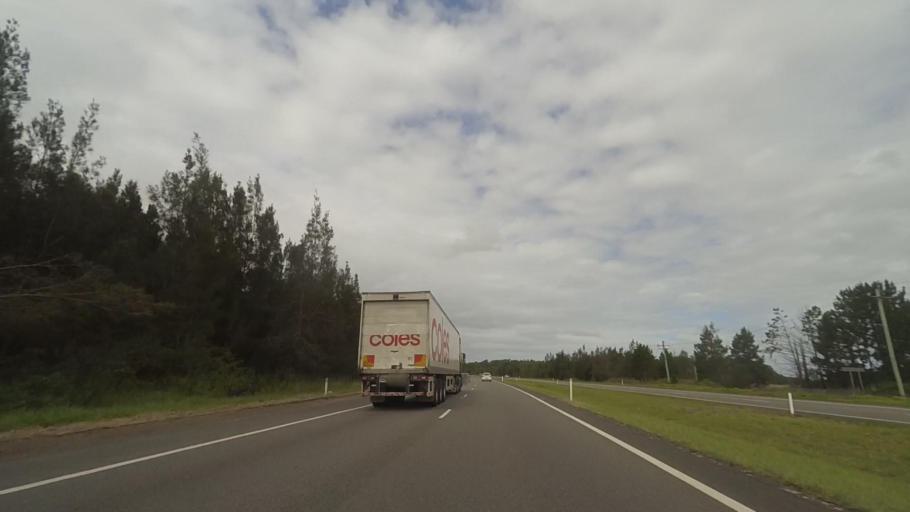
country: AU
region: New South Wales
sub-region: Port Stephens Shire
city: Raymond Terrace
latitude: -32.7780
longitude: 151.7519
